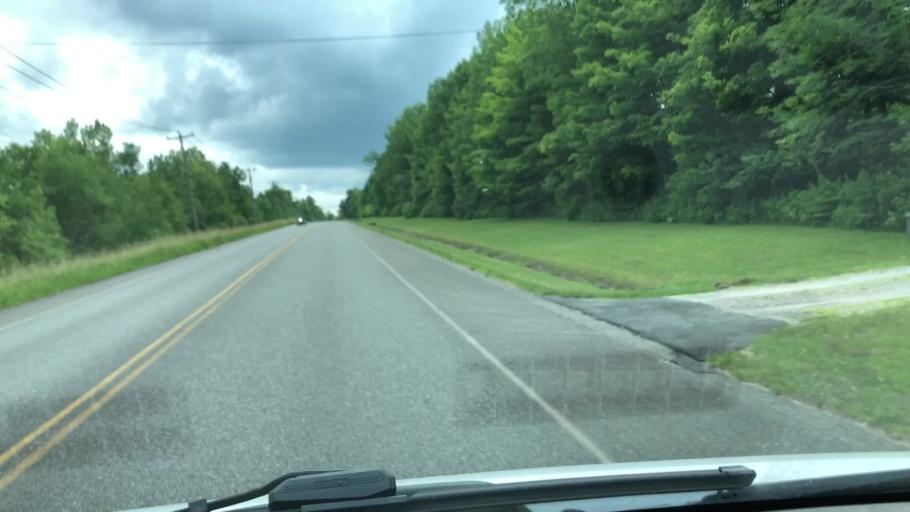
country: US
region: Massachusetts
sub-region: Berkshire County
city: Adams
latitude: 42.5504
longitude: -73.0471
